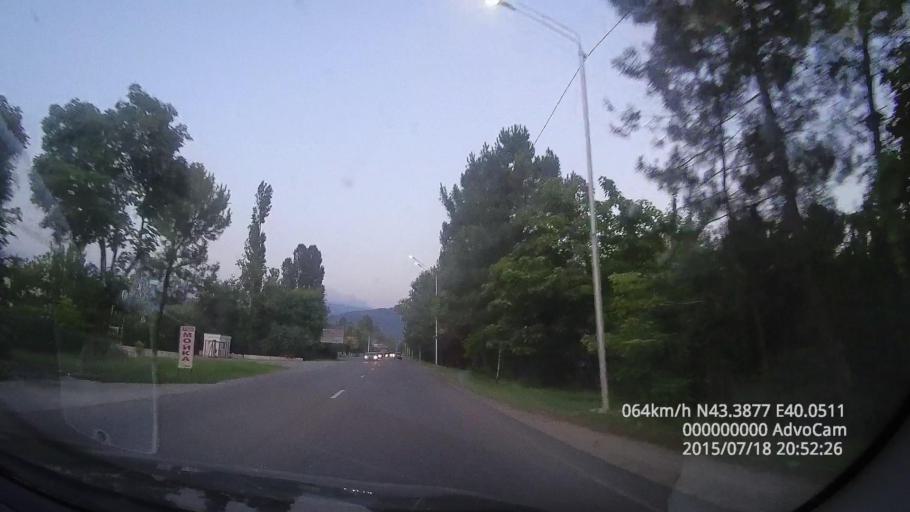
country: GE
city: Gantiadi
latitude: 43.3875
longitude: 40.0526
